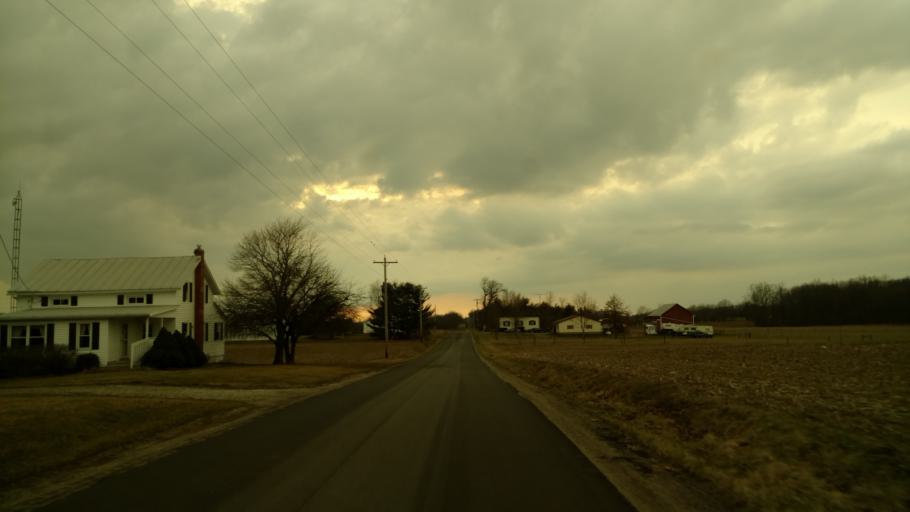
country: US
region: Ohio
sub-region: Crawford County
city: Galion
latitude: 40.6239
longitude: -82.7124
